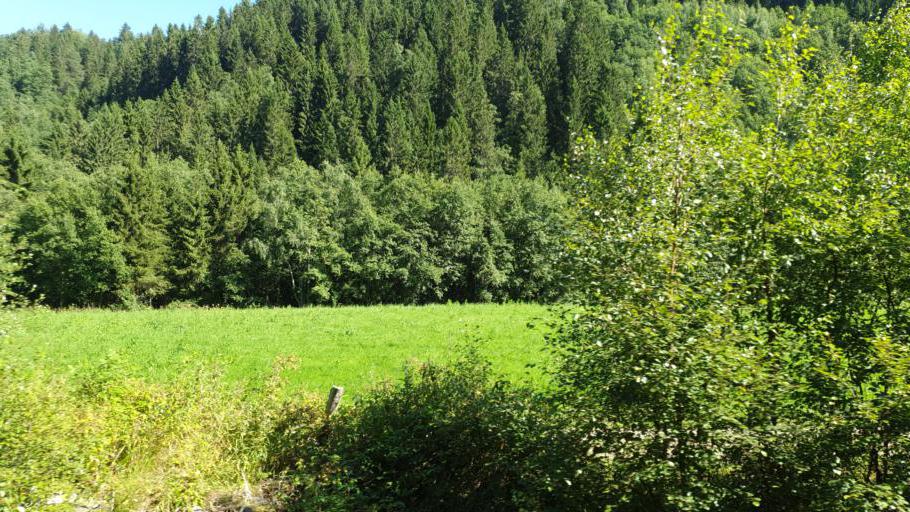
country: NO
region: Sor-Trondelag
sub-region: Orkdal
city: Orkanger
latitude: 63.1935
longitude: 9.7845
